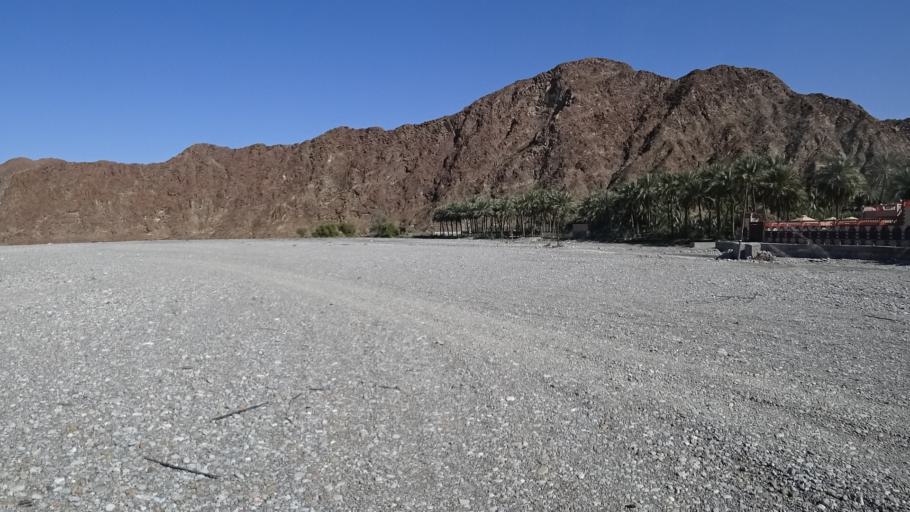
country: OM
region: Al Batinah
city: Bayt al `Awabi
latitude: 23.3907
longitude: 57.6619
